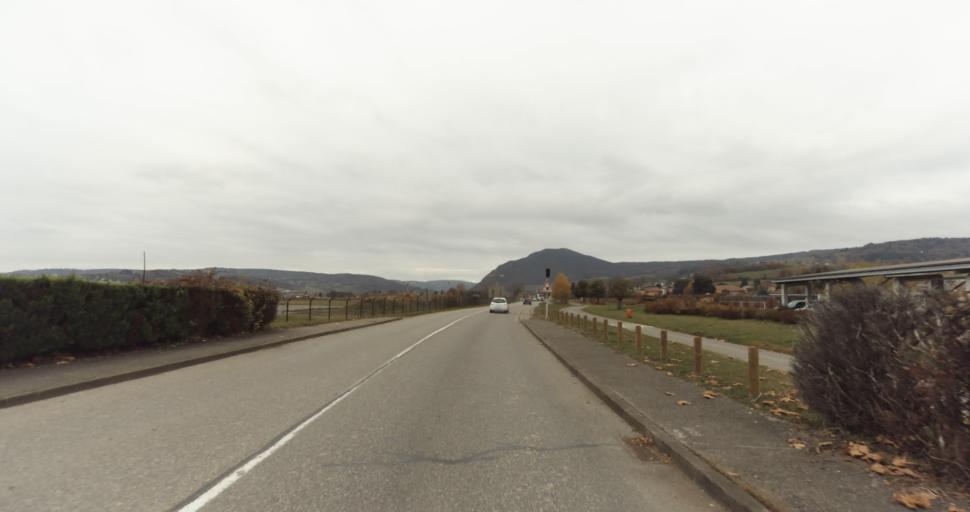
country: FR
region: Rhone-Alpes
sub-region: Departement de la Haute-Savoie
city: Metz-Tessy
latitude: 45.9351
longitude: 6.1068
